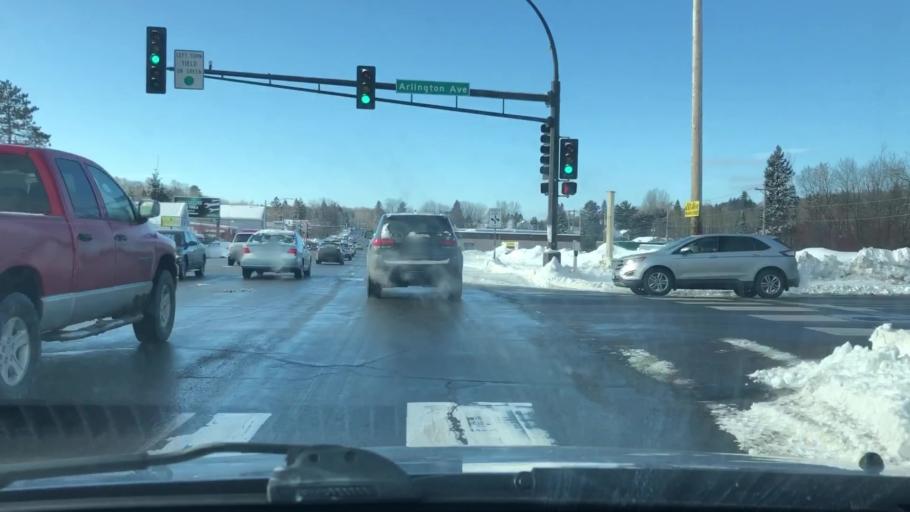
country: US
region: Minnesota
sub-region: Saint Louis County
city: Duluth
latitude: 46.8005
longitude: -92.1320
